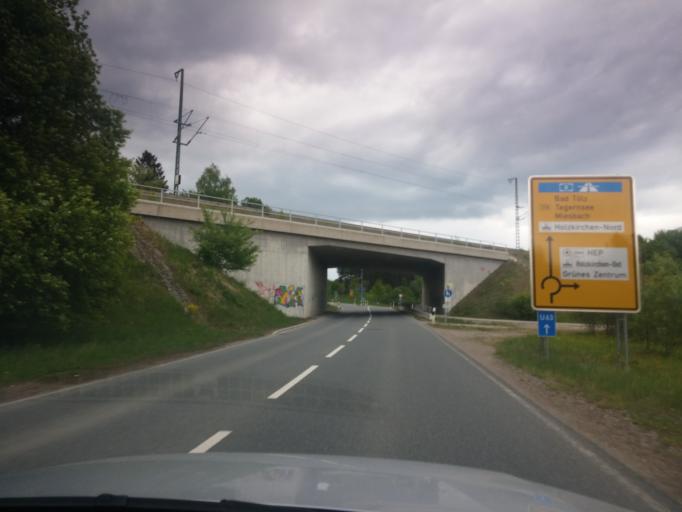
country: DE
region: Bavaria
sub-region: Upper Bavaria
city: Holzkirchen
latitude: 47.8875
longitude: 11.7142
